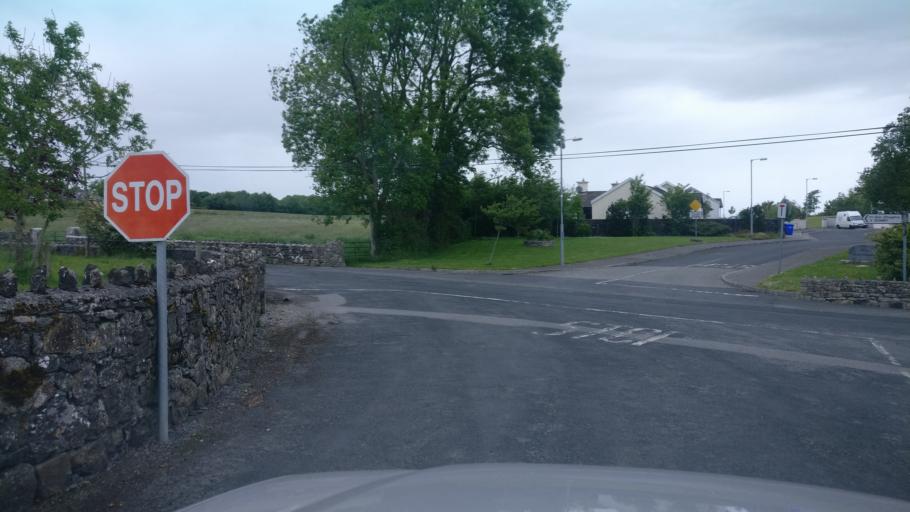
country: IE
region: Connaught
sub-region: County Galway
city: Portumna
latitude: 53.1046
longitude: -8.3942
